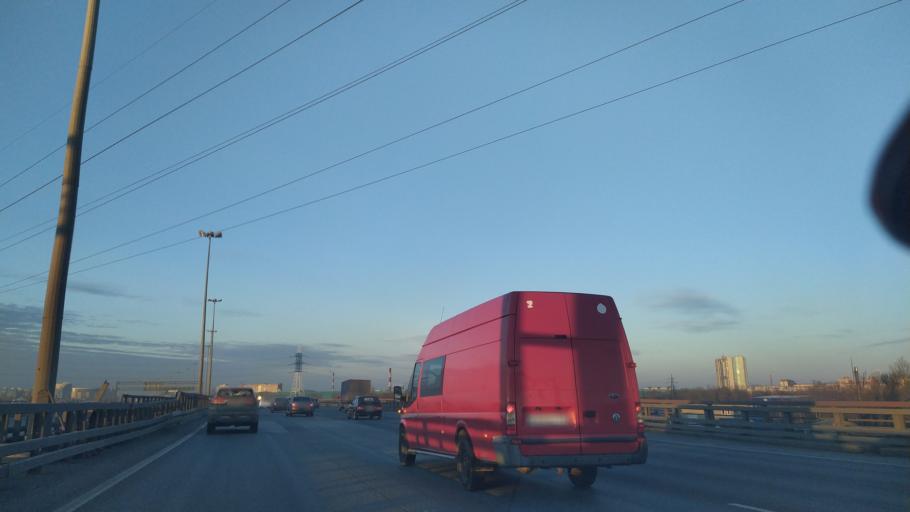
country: RU
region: St.-Petersburg
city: Obukhovo
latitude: 59.8384
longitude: 30.4531
